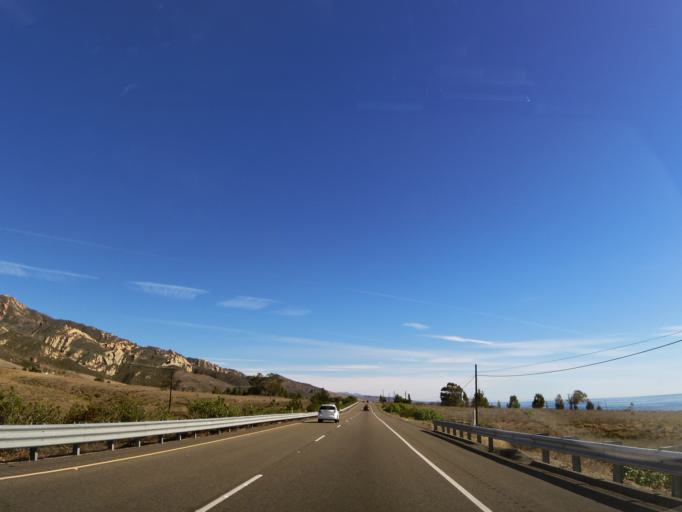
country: US
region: California
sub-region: Santa Barbara County
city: Buellton
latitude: 34.4732
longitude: -120.2205
